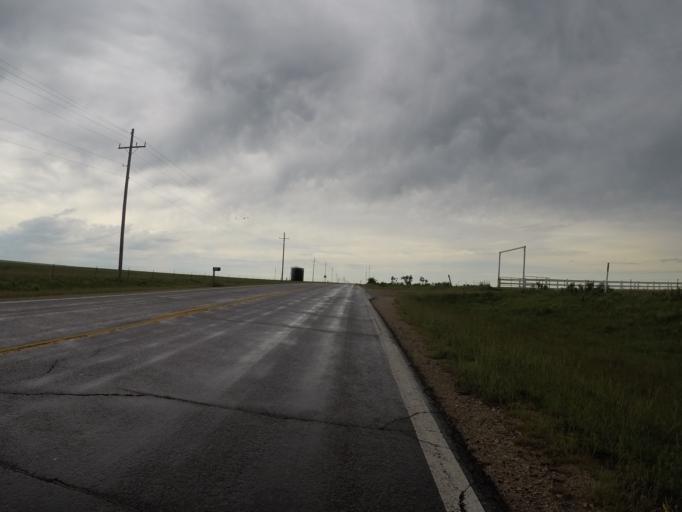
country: US
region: Kansas
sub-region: Wabaunsee County
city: Alma
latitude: 38.8637
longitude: -96.1185
